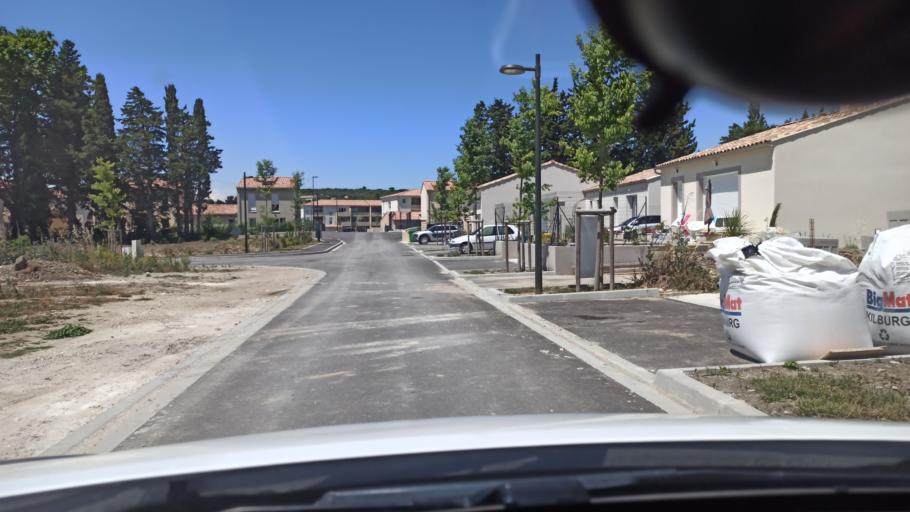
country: FR
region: Provence-Alpes-Cote d'Azur
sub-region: Departement du Vaucluse
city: Caumont-sur-Durance
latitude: 43.8945
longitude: 4.9542
